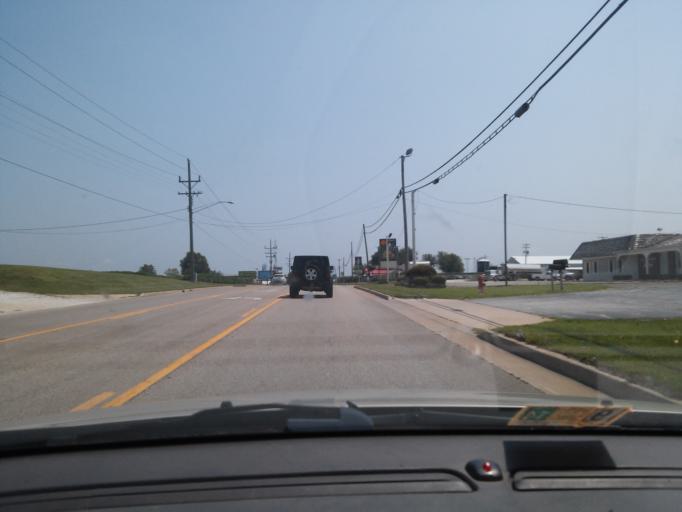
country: US
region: Illinois
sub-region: Pike County
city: Pittsfield
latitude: 39.6046
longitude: -90.8404
